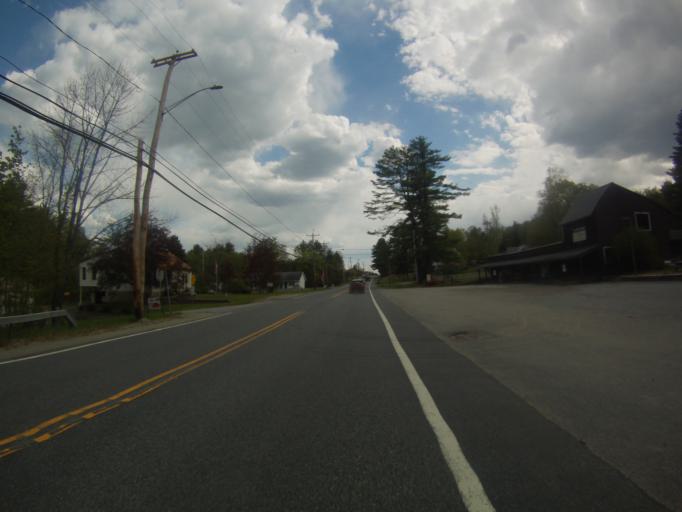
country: US
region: New York
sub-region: Essex County
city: Ticonderoga
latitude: 43.8567
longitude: -73.7560
